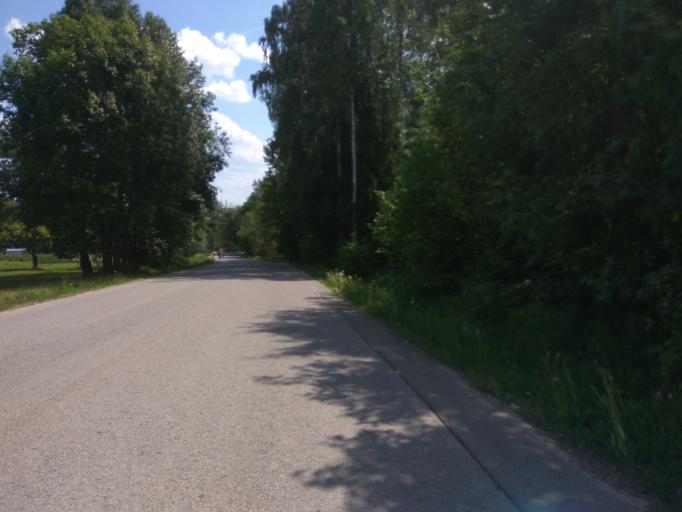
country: LV
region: Kuldigas Rajons
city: Kuldiga
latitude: 56.9154
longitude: 21.9651
